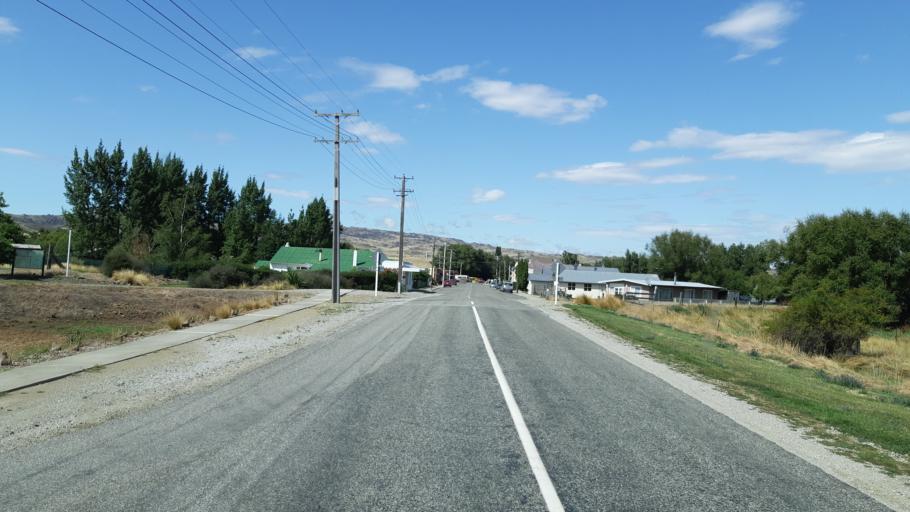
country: NZ
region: Otago
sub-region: Queenstown-Lakes District
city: Wanaka
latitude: -45.0918
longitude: 169.6019
